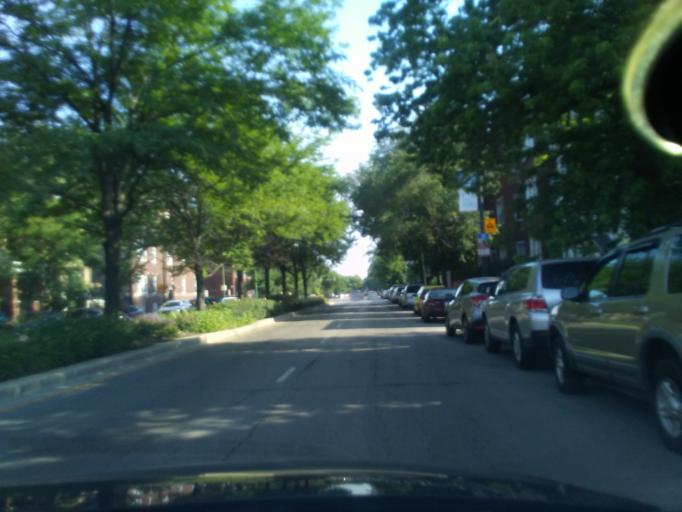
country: US
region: Illinois
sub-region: Cook County
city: Lincolnwood
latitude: 41.9751
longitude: -87.6697
